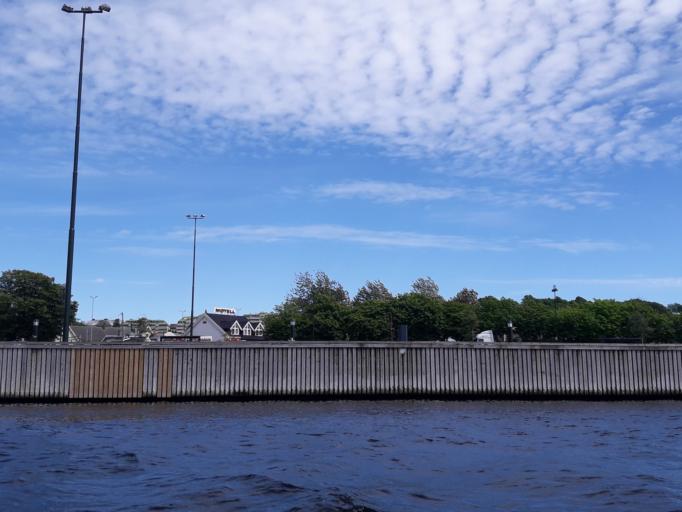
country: NO
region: Ostfold
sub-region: Moss
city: Moss
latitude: 59.4312
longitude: 10.6530
